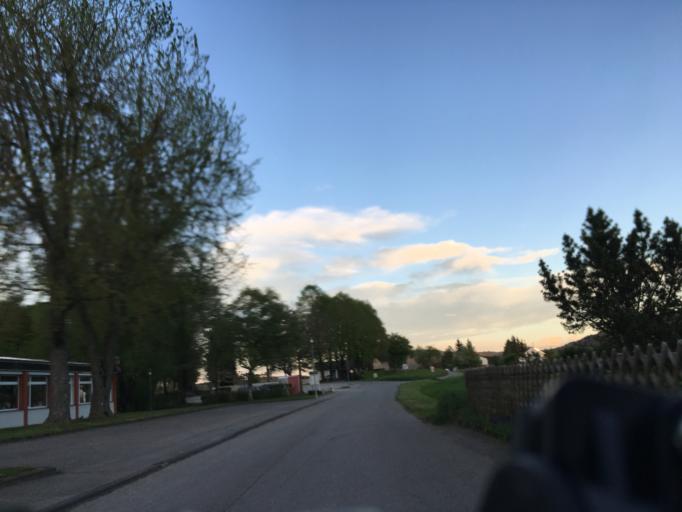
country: DE
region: Baden-Wuerttemberg
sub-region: Freiburg Region
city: Gottmadingen
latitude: 47.7222
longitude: 8.7581
